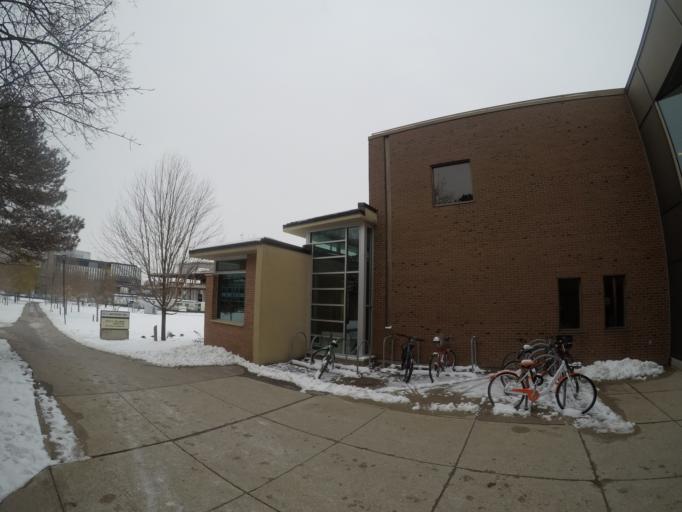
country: CA
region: Ontario
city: Waterloo
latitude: 43.4735
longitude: -80.5452
